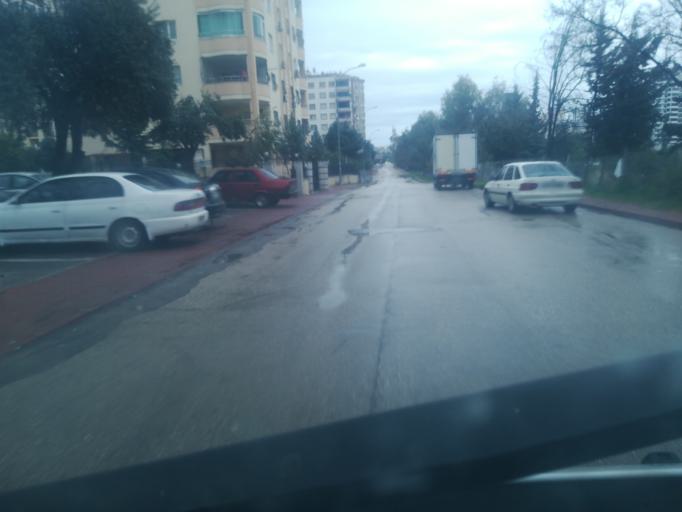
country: TR
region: Adana
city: Seyhan
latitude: 37.0309
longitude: 35.2783
